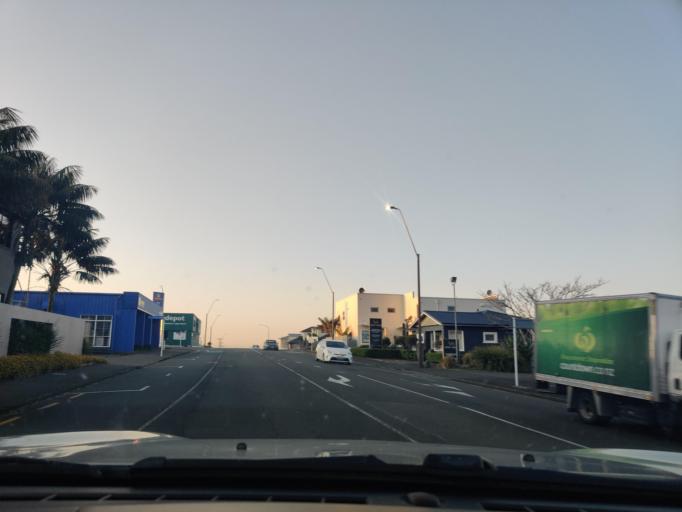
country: NZ
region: Taranaki
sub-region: New Plymouth District
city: New Plymouth
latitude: -39.0539
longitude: 174.0865
